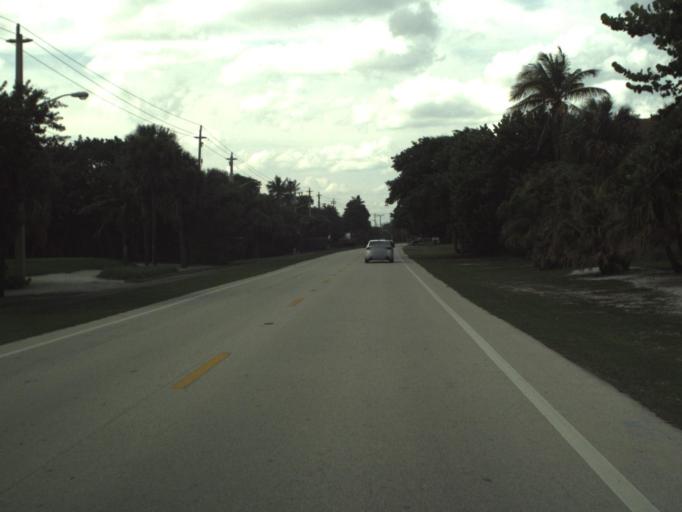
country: US
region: Florida
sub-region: Palm Beach County
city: Lake Worth
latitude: 26.6340
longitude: -80.0392
